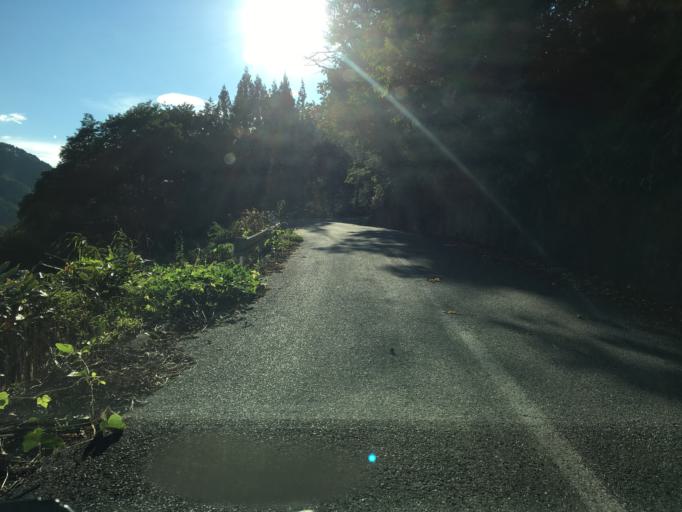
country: JP
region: Yamagata
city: Yonezawa
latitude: 37.8619
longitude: 140.1631
